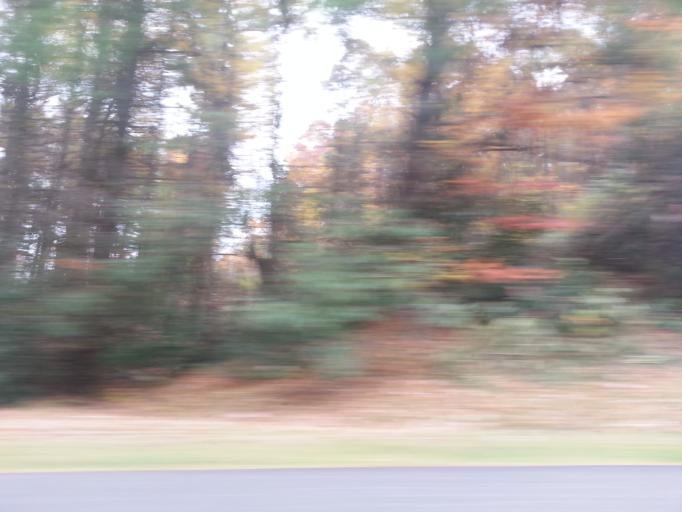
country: US
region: North Carolina
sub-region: Ashe County
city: Jefferson
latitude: 36.3123
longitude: -81.3622
